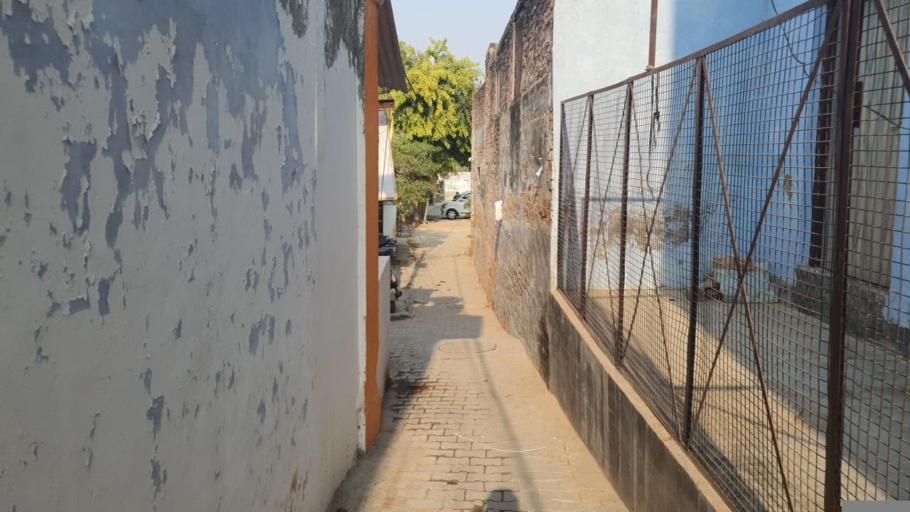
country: IN
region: Uttar Pradesh
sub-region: Lucknow District
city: Lucknow
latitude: 26.7983
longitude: 81.0075
